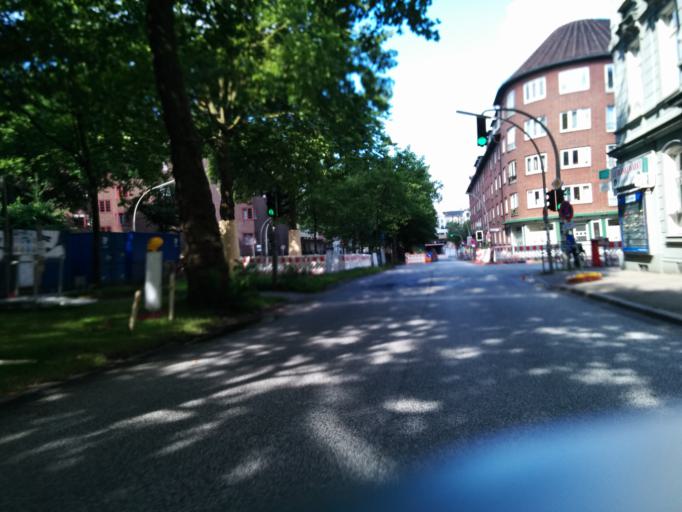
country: DE
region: Hamburg
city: Altona
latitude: 53.5556
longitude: 9.9389
